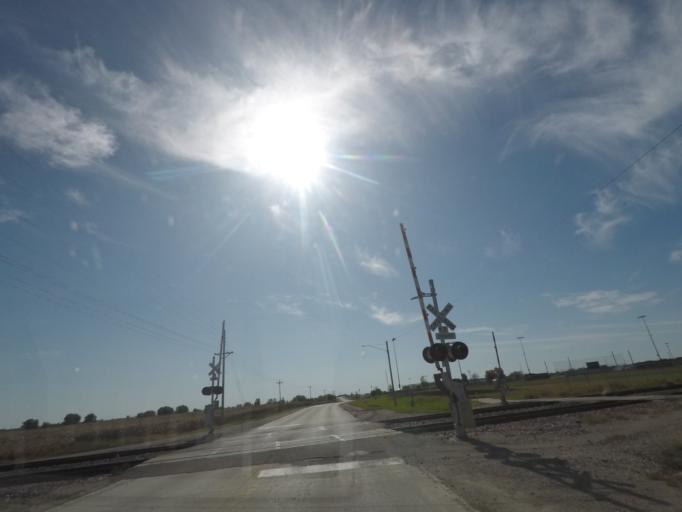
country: US
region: Iowa
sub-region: Story County
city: Nevada
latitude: 42.0165
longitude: -93.4347
